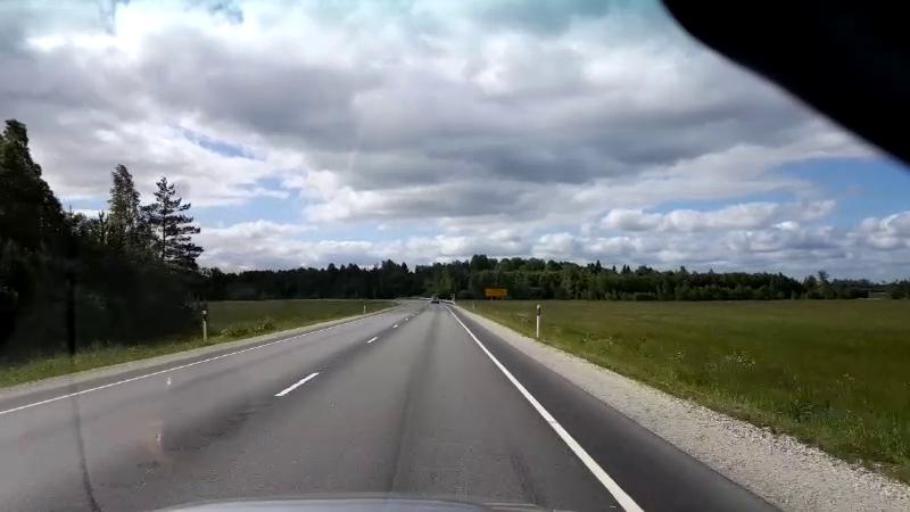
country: EE
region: Paernumaa
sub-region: Halinga vald
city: Parnu-Jaagupi
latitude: 58.6747
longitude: 24.4436
